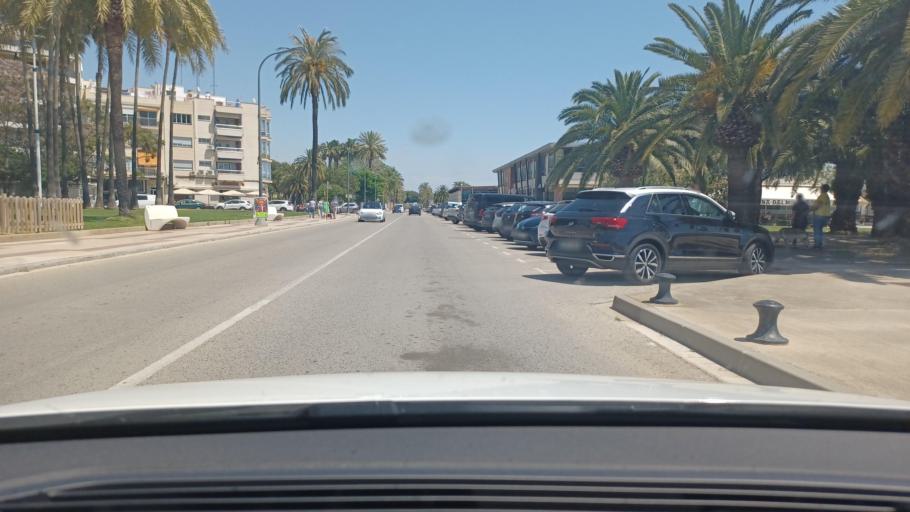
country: ES
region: Catalonia
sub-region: Provincia de Tarragona
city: Sant Carles de la Rapita
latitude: 40.6173
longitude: 0.5942
